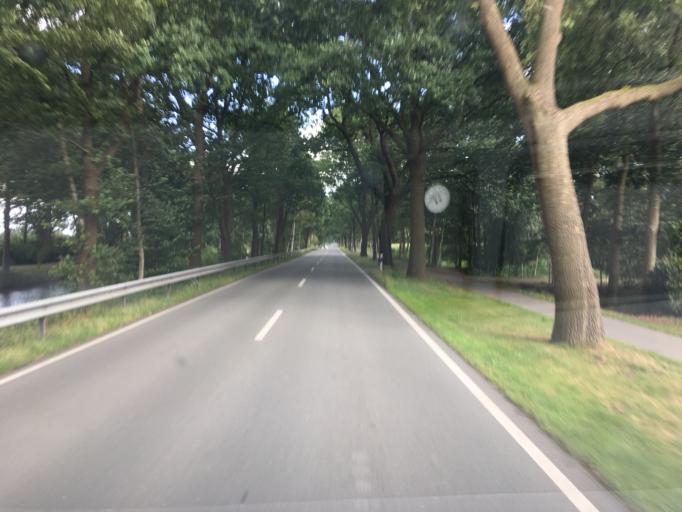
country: DE
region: Lower Saxony
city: Friesoythe
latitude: 53.0855
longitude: 7.8077
